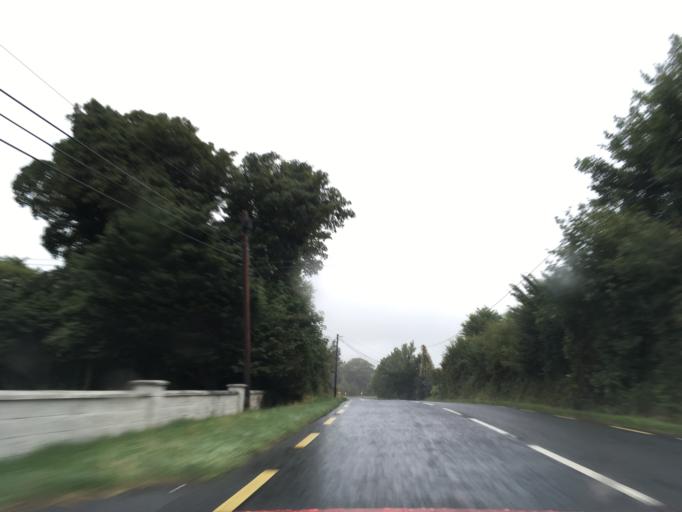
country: IE
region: Munster
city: Tipperary
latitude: 52.4808
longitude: -8.1124
